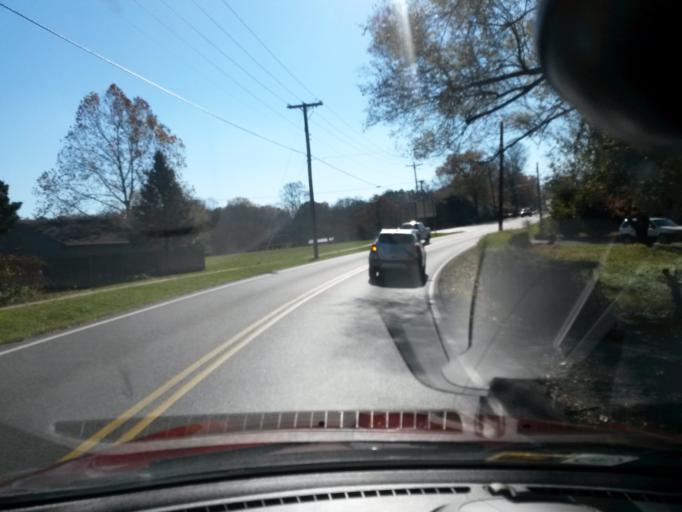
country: US
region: Virginia
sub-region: City of Bedford
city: Bedford
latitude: 37.3504
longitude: -79.5271
